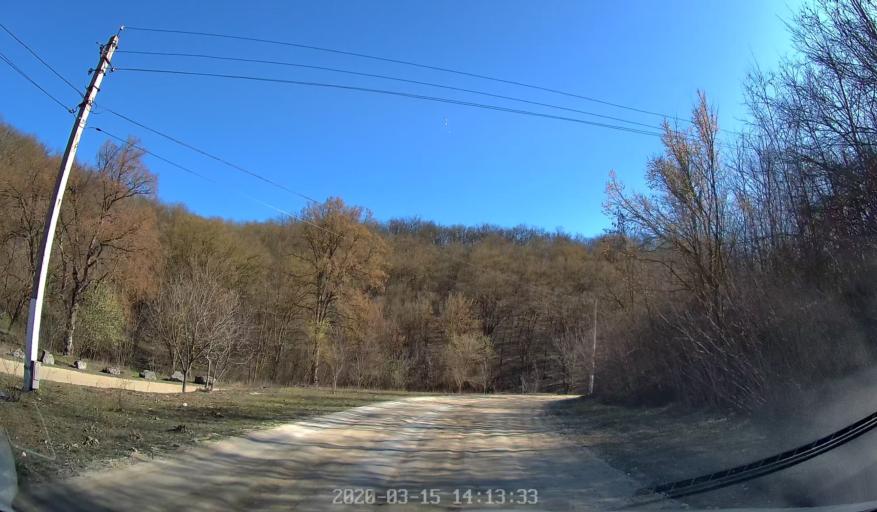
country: MD
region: Orhei
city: Orhei
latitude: 47.3144
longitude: 28.9377
